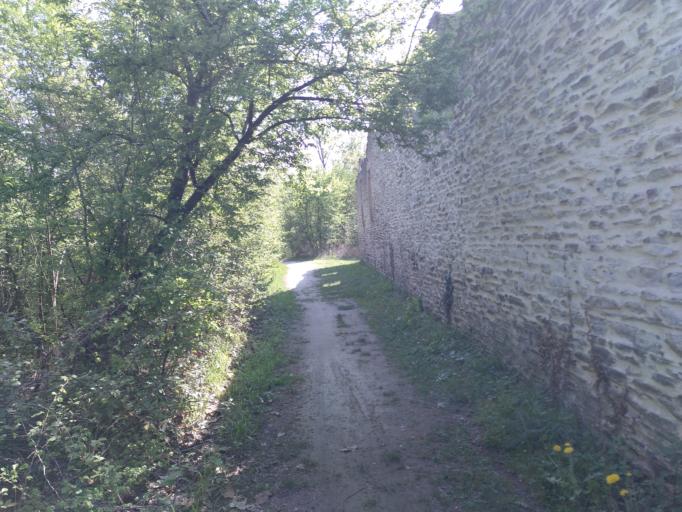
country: FR
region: Rhone-Alpes
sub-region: Departement du Rhone
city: Serezin-du-Rhone
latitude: 45.6307
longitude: 4.8095
